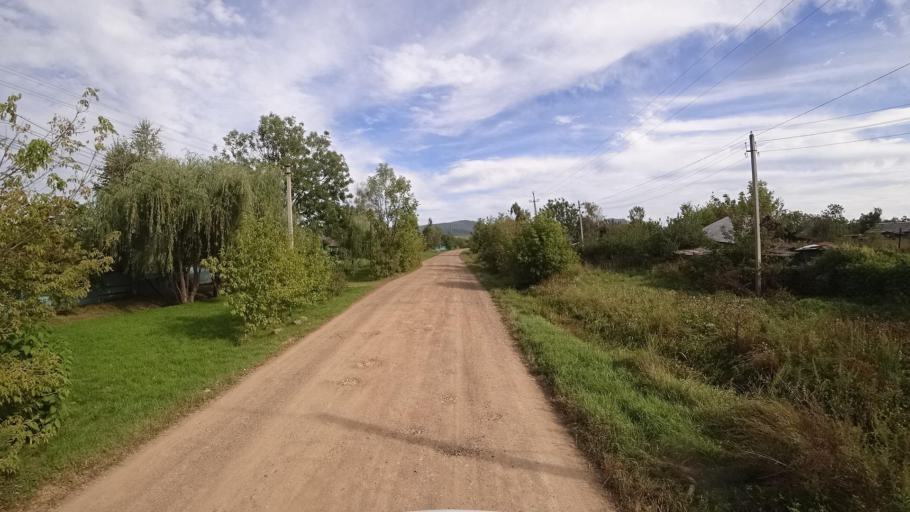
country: RU
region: Primorskiy
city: Dostoyevka
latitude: 44.3061
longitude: 133.4583
